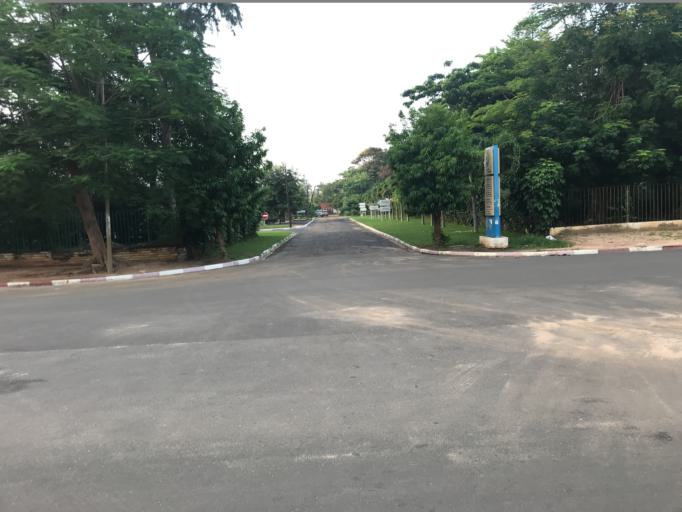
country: SN
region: Dakar
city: Mermoz Boabab
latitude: 14.6855
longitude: -17.4679
